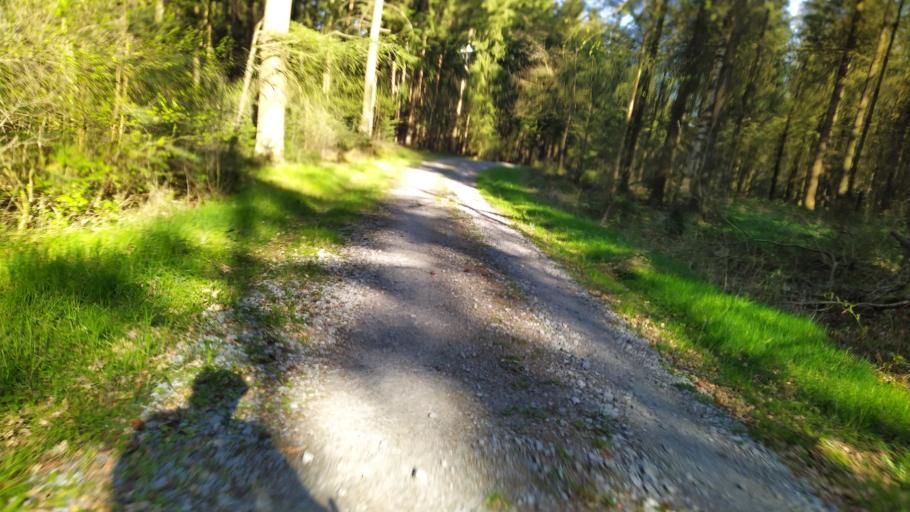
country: DE
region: Lower Saxony
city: Klein Meckelsen
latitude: 53.2944
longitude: 9.4679
